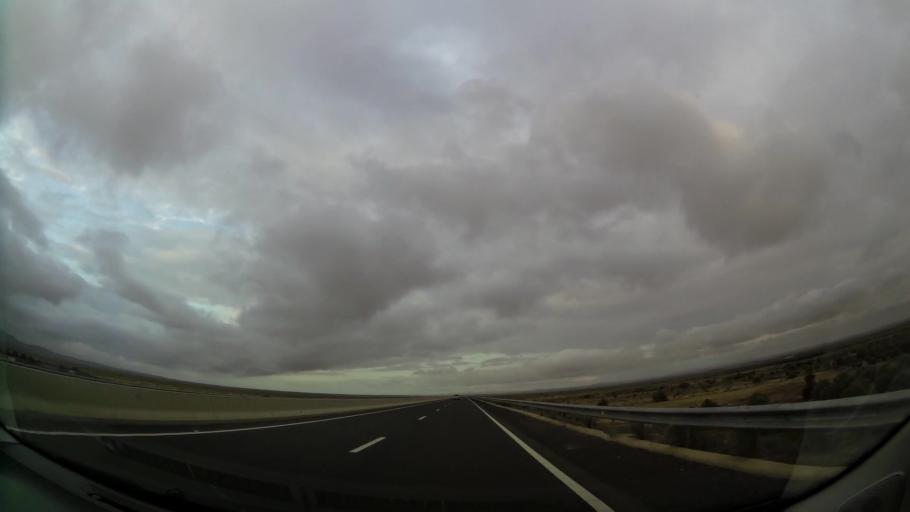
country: MA
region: Taza-Al Hoceima-Taounate
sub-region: Taza
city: Guercif
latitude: 34.3637
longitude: -3.2883
